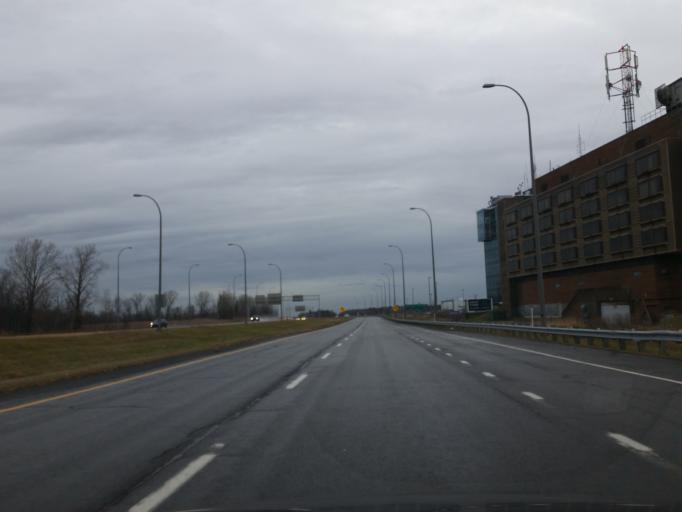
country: CA
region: Quebec
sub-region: Laurentides
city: Mirabel
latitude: 45.6840
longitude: -74.0330
